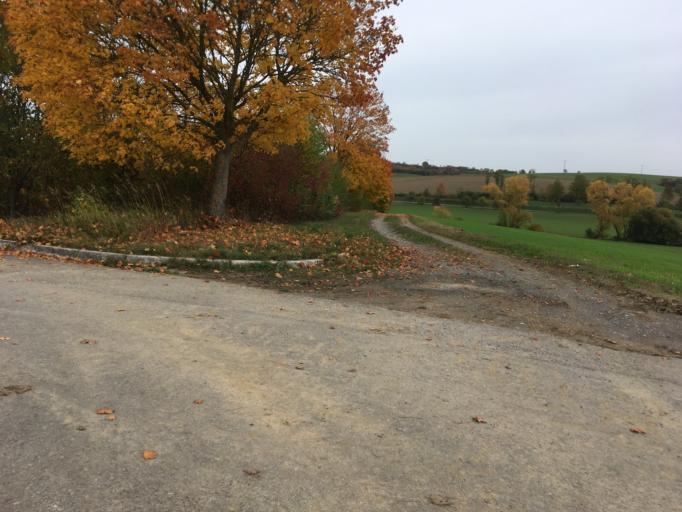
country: DE
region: Baden-Wuerttemberg
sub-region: Karlsruhe Region
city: Buchen
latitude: 49.5076
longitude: 9.3245
